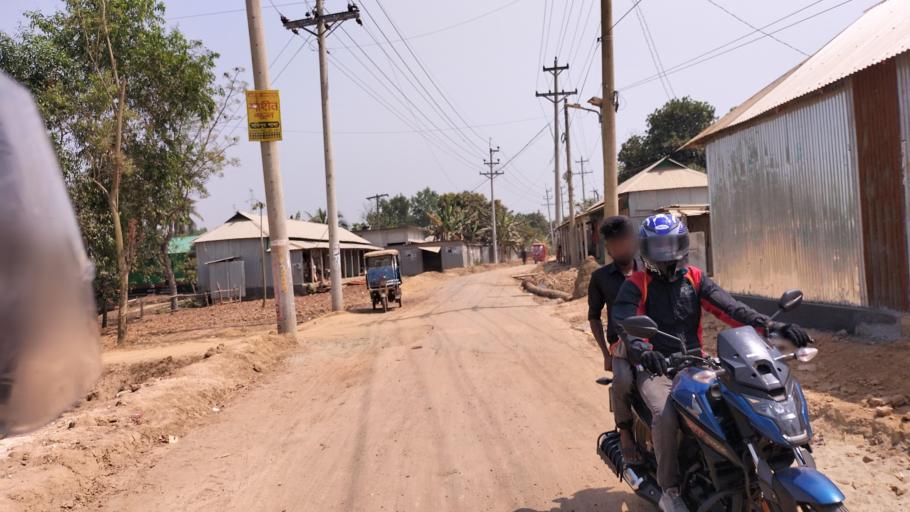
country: BD
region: Dhaka
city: Sakhipur
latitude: 24.3093
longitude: 90.2920
